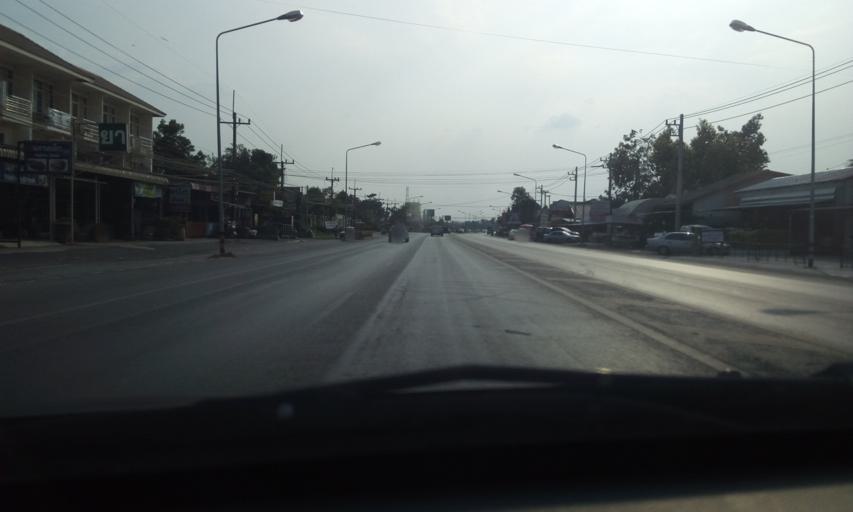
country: TH
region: Nakhon Nayok
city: Nakhon Nayok
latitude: 14.2230
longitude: 101.2325
